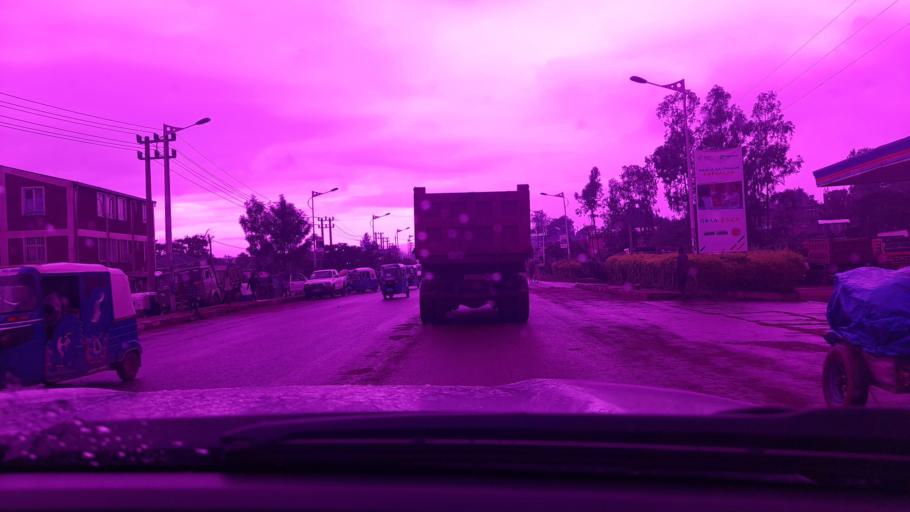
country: ET
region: Oromiya
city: Jima
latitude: 7.6681
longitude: 36.8456
